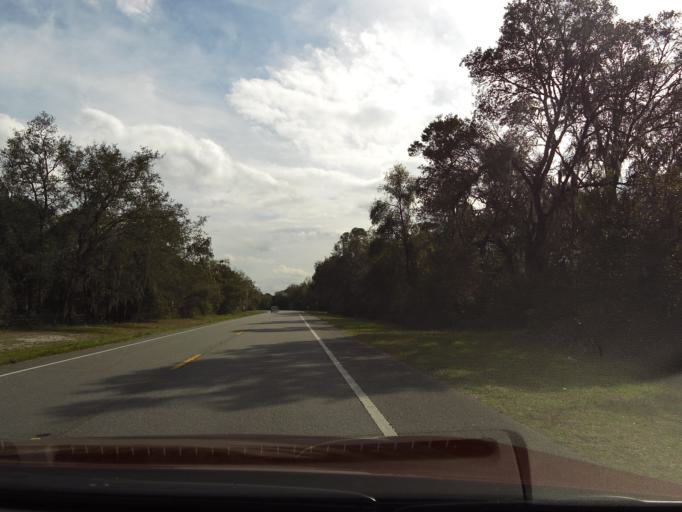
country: US
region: Florida
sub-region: Volusia County
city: De Leon Springs
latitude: 29.1762
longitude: -81.3029
